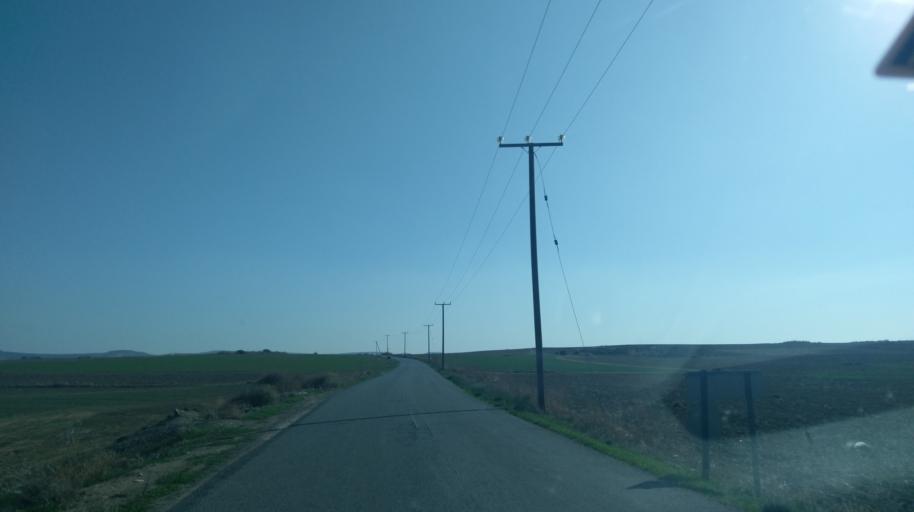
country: CY
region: Larnaka
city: Athienou
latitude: 35.1051
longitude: 33.5659
